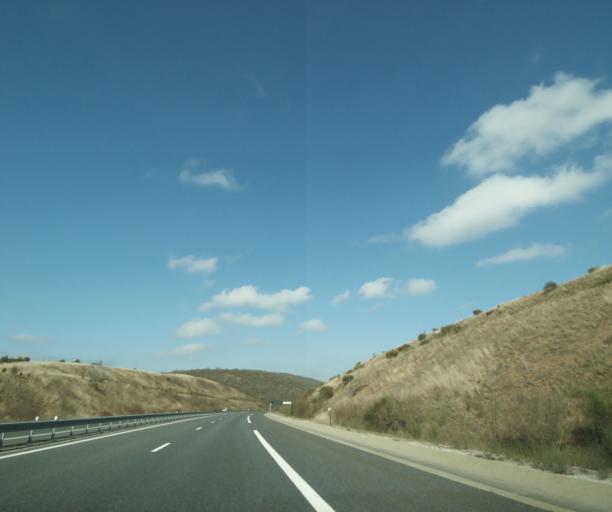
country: FR
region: Midi-Pyrenees
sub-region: Departement de l'Aveyron
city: Creissels
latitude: 44.0601
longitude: 3.0299
